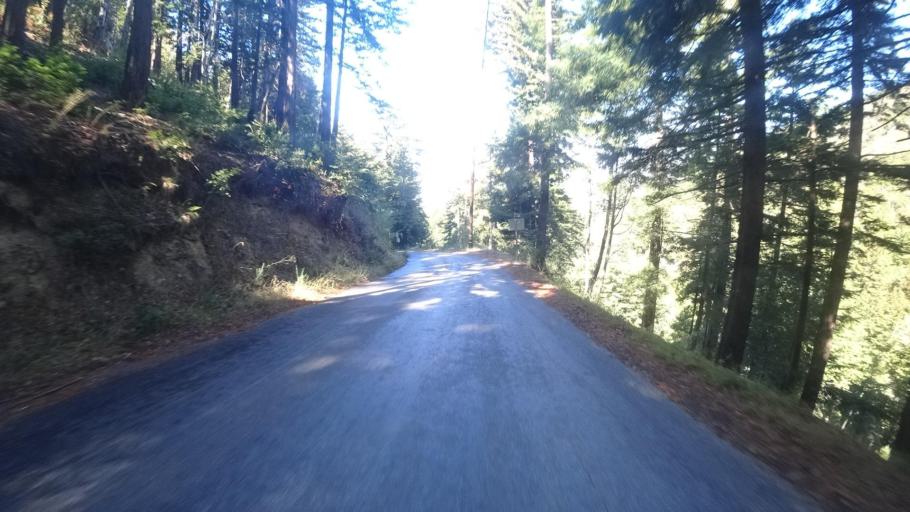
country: US
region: California
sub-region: Monterey County
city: Carmel Valley Village
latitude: 36.3790
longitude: -121.8600
